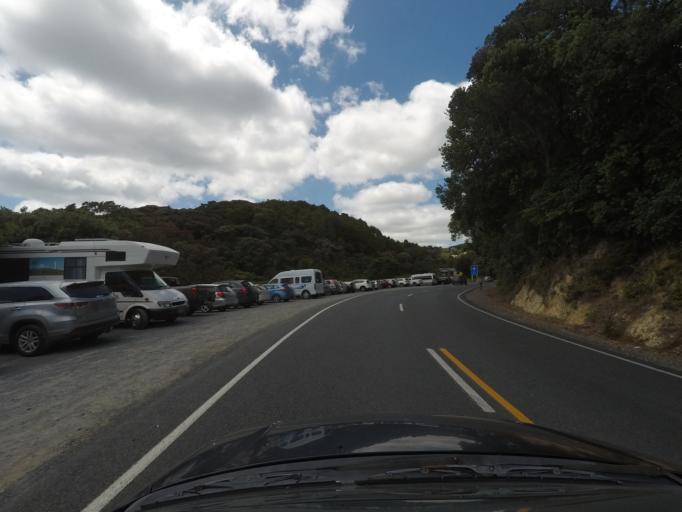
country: NZ
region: Northland
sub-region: Whangarei
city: Ruakaka
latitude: -36.0306
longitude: 174.5087
